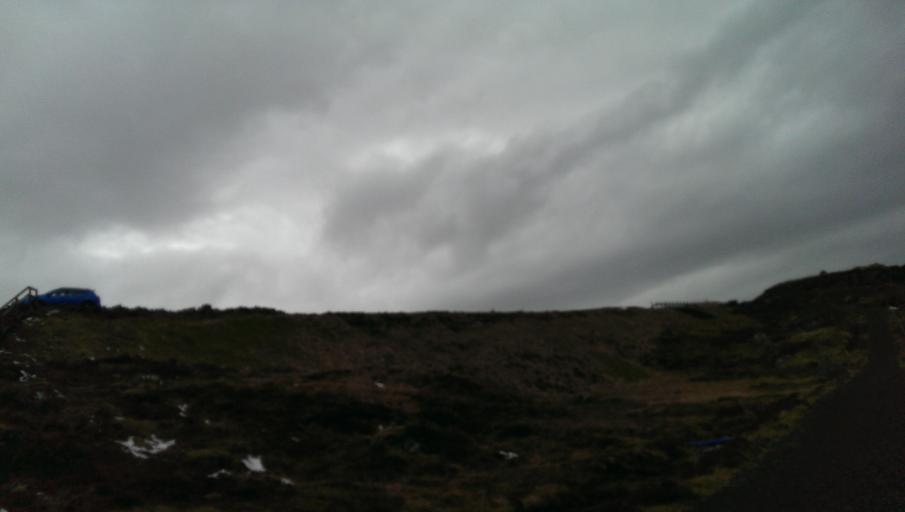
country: FO
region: Streymoy
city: Hoyvik
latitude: 62.0319
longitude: -6.7959
